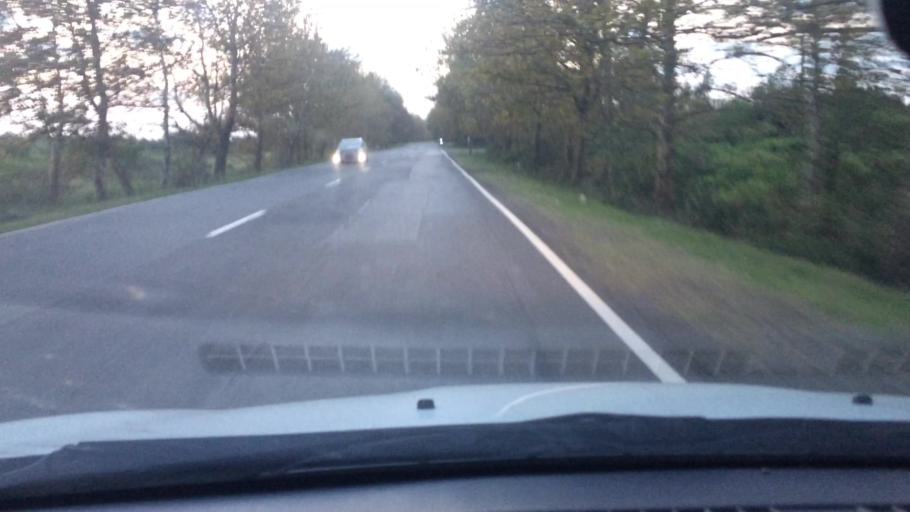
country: GE
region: Guria
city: Urek'i
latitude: 42.0179
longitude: 41.7660
